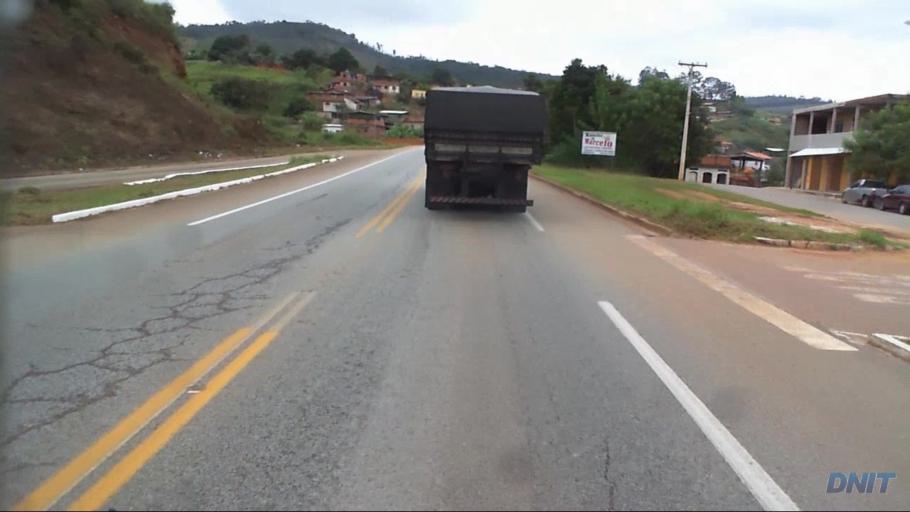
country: BR
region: Minas Gerais
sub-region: Joao Monlevade
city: Joao Monlevade
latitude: -19.8265
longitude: -43.0856
